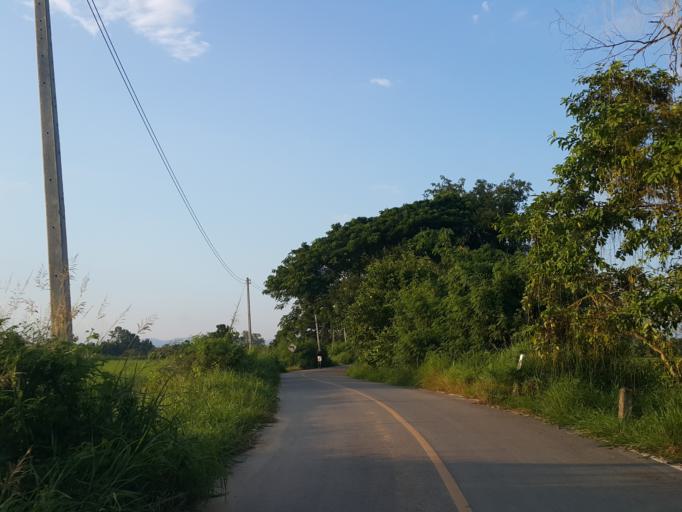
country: TH
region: Chiang Mai
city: San Kamphaeng
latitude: 18.7767
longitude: 99.1075
